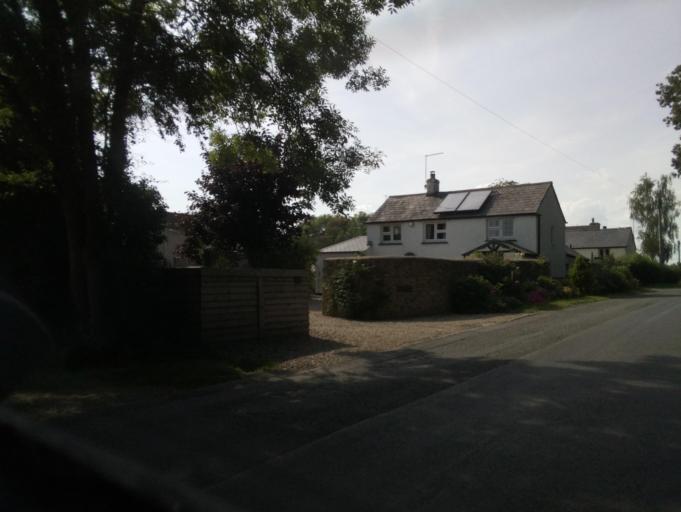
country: GB
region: England
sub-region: Wiltshire
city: Minety
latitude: 51.6160
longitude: -1.9653
